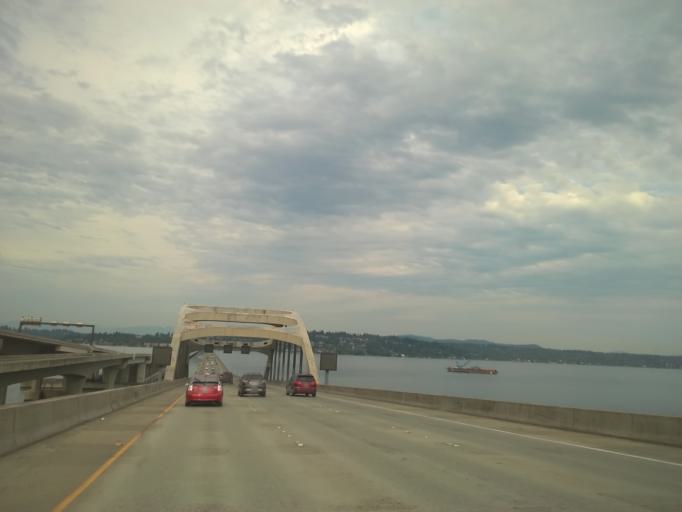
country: US
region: Washington
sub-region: King County
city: Seattle
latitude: 47.5899
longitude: -122.2844
